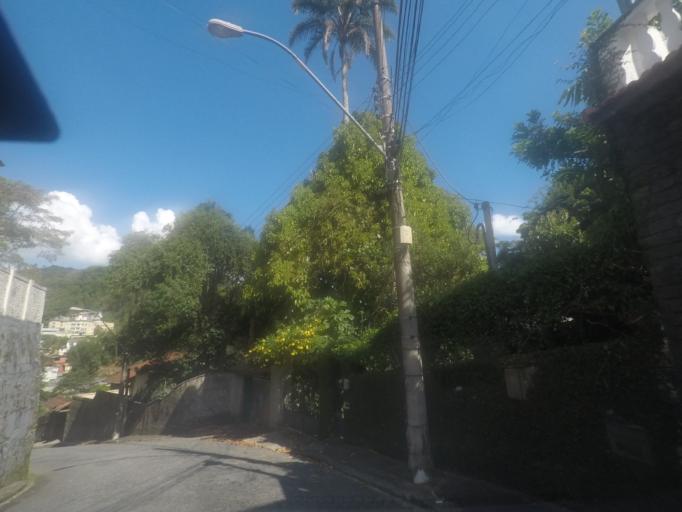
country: BR
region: Rio de Janeiro
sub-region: Petropolis
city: Petropolis
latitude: -22.5193
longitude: -43.1887
